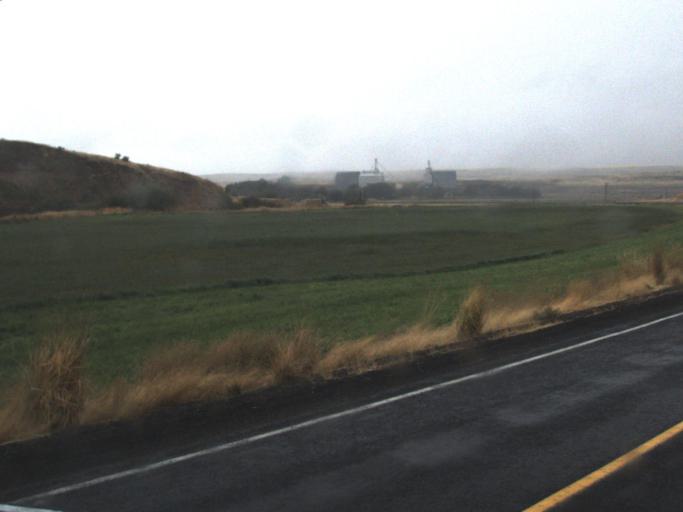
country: US
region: Washington
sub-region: Spokane County
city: Cheney
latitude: 47.1148
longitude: -117.7152
